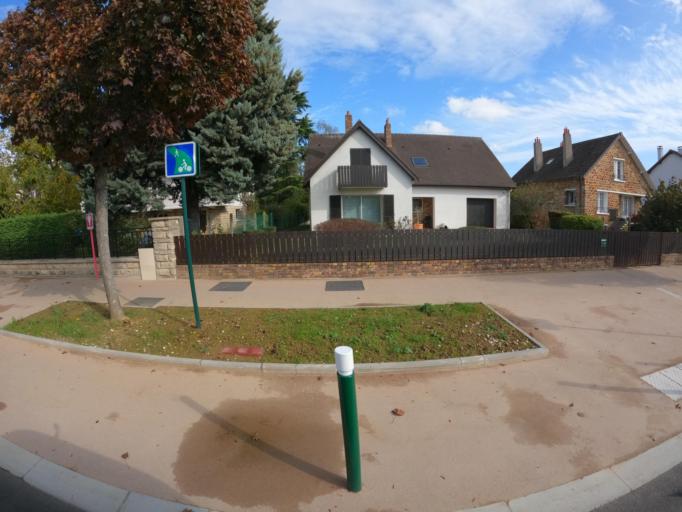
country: FR
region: Ile-de-France
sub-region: Departement de Seine-et-Marne
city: Vaires-sur-Marne
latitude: 48.8786
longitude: 2.6361
